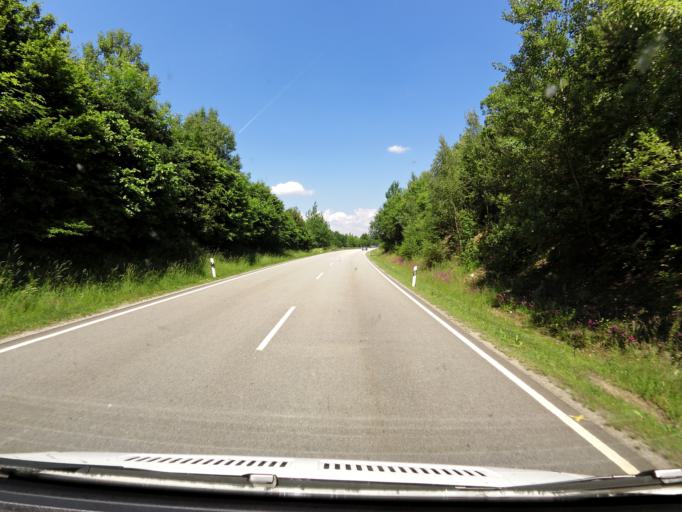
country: DE
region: Bavaria
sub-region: Lower Bavaria
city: Roehrnbach
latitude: 48.7599
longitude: 13.5106
